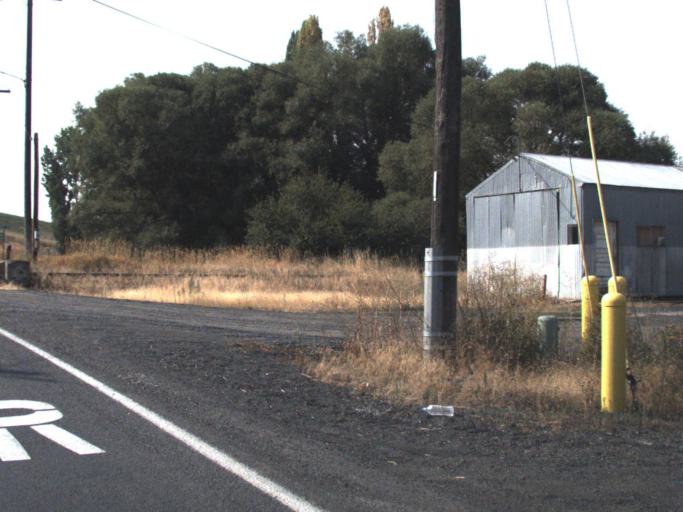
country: US
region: Idaho
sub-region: Latah County
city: Moscow
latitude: 46.9074
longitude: -117.0801
